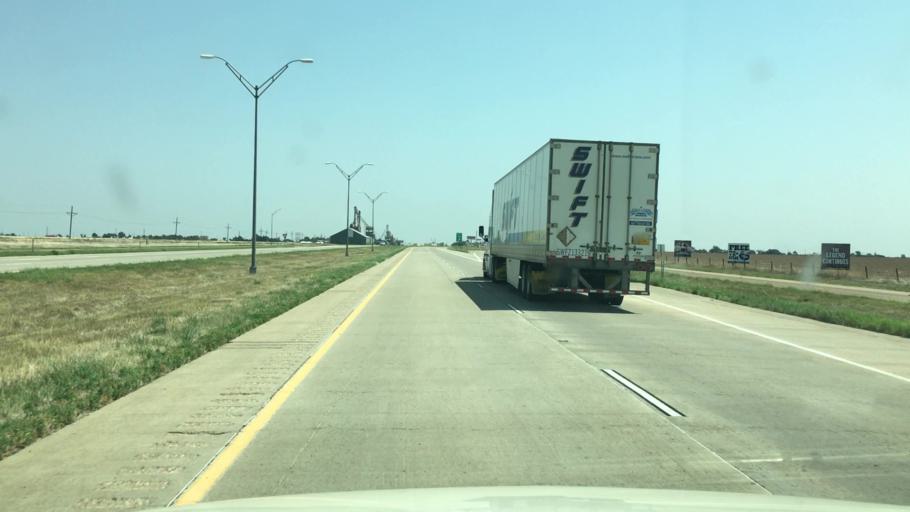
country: US
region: Texas
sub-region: Potter County
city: Bushland
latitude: 35.2097
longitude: -102.2200
